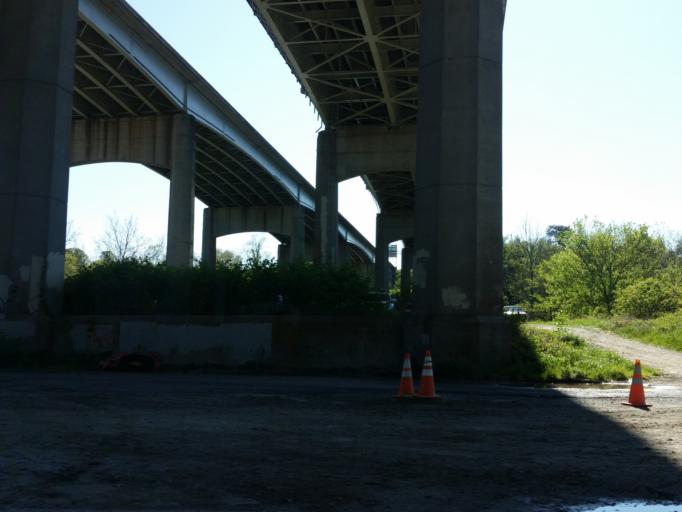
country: US
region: North Carolina
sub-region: Buncombe County
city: Asheville
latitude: 35.5911
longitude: -82.5713
